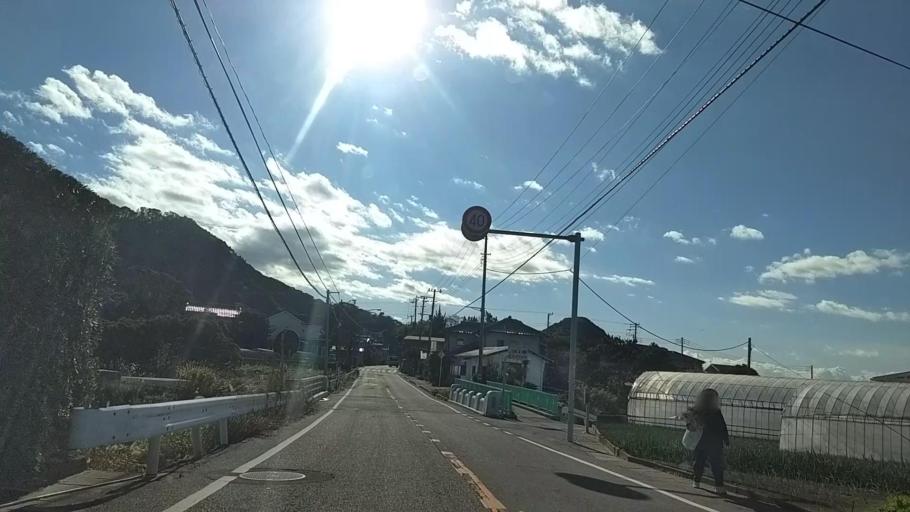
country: JP
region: Chiba
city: Tateyama
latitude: 35.0597
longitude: 139.8279
